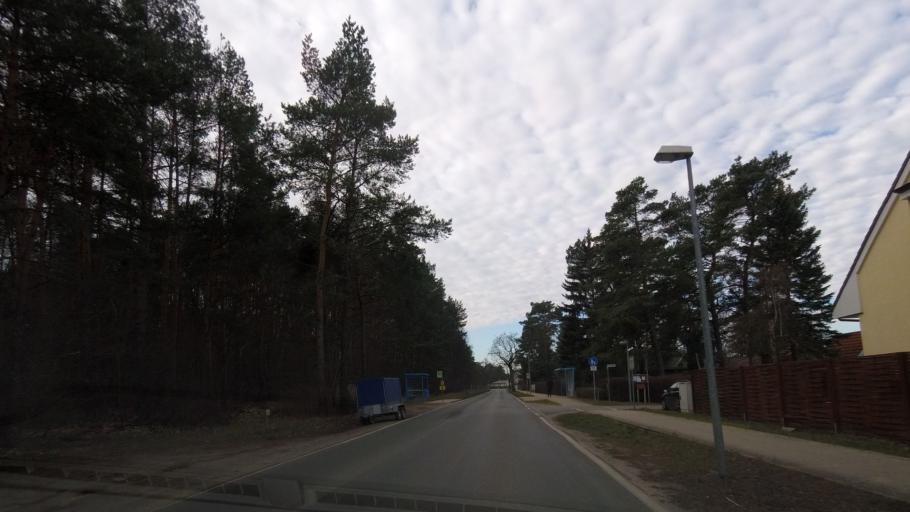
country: DE
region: Berlin
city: Schmockwitz
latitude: 52.3585
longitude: 13.6806
